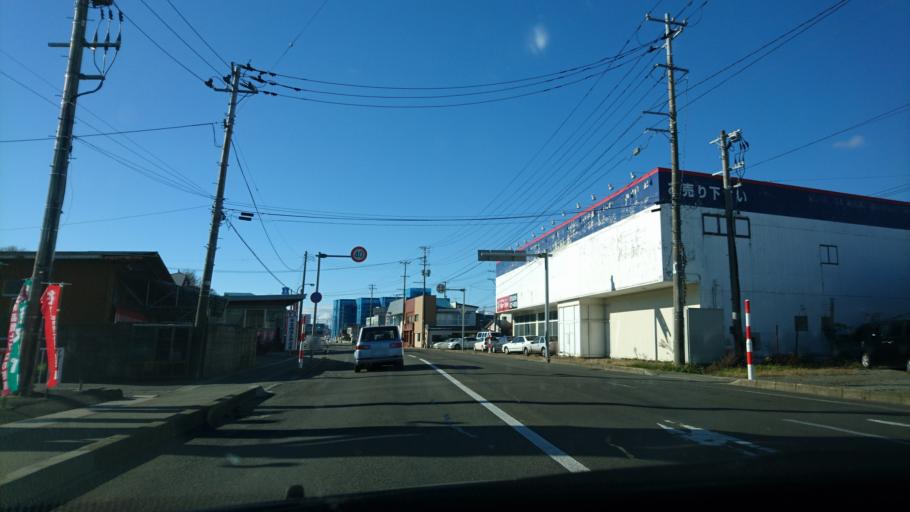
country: JP
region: Akita
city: Akita Shi
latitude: 39.3861
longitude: 140.0422
